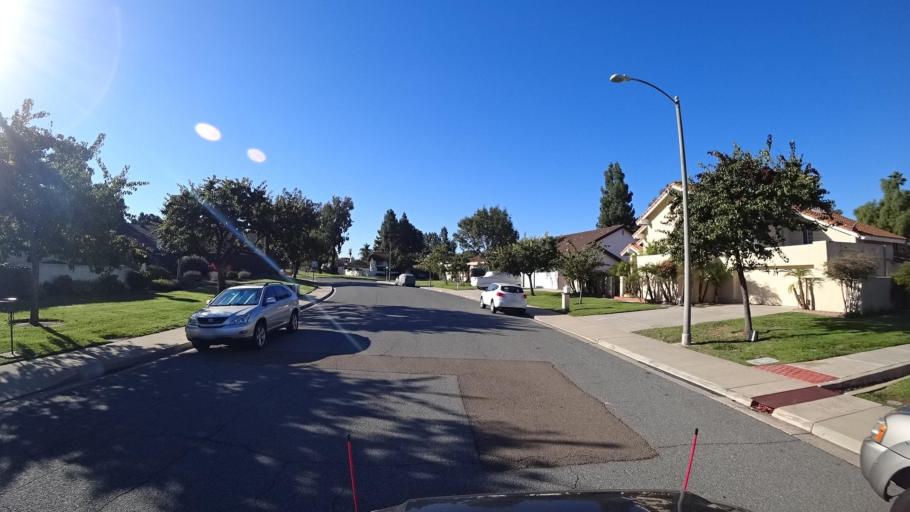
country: US
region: California
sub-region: San Diego County
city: Bonita
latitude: 32.6754
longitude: -117.0277
